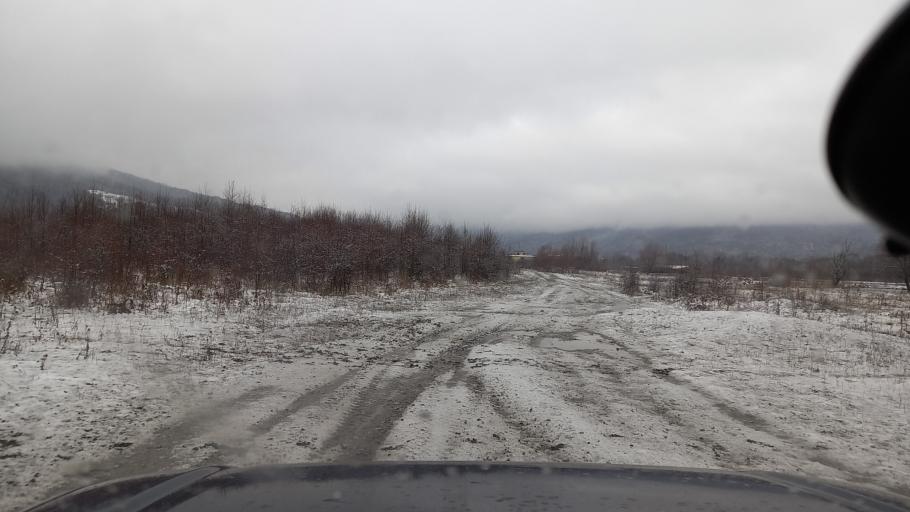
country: RU
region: Adygeya
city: Kamennomostskiy
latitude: 44.2266
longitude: 40.1794
